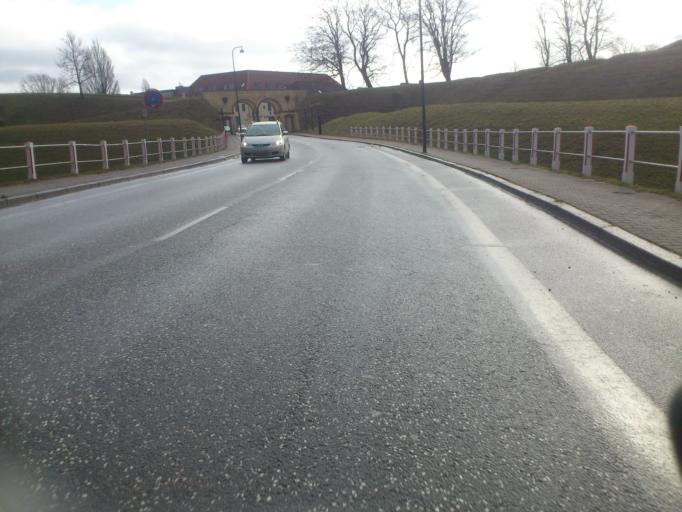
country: DK
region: South Denmark
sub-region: Fredericia Kommune
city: Fredericia
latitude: 55.5681
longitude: 9.7506
